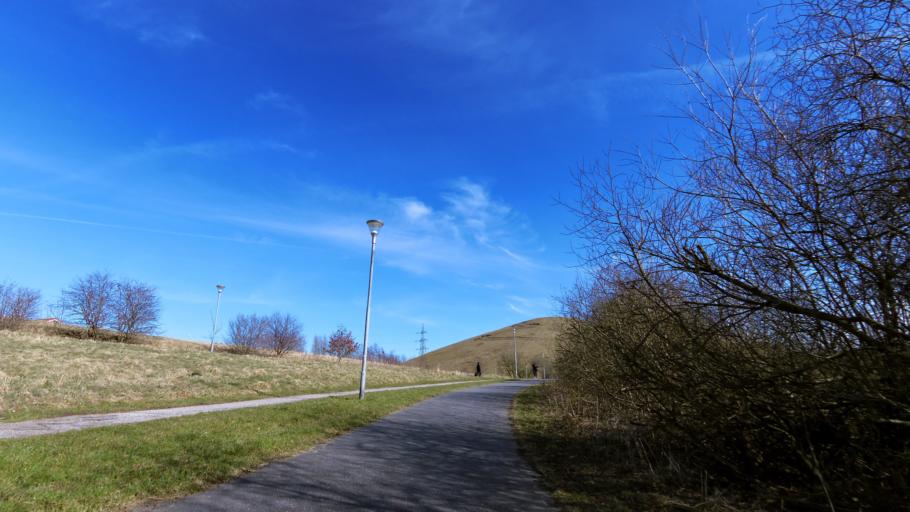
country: DK
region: Central Jutland
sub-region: Arhus Kommune
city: Stavtrup
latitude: 56.1696
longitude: 10.1384
